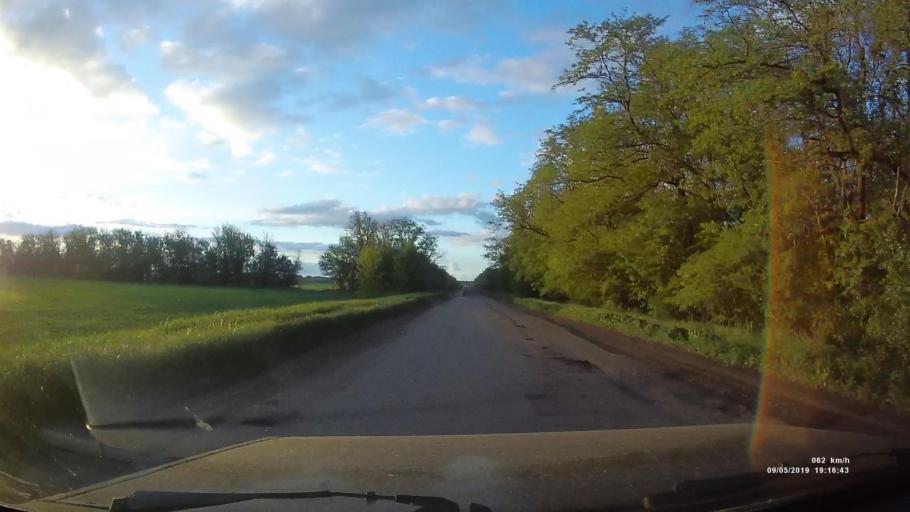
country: RU
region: Krasnodarskiy
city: Kanelovskaya
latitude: 46.7802
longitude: 39.2116
